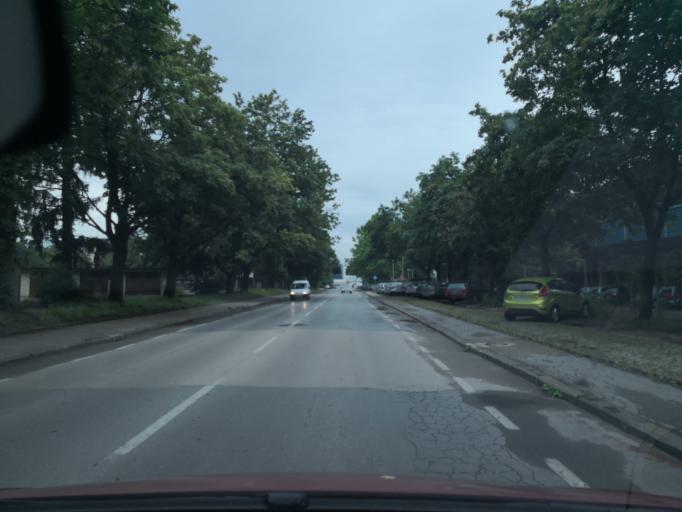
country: SI
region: Ljubljana
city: Ljubljana
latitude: 46.0635
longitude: 14.5327
